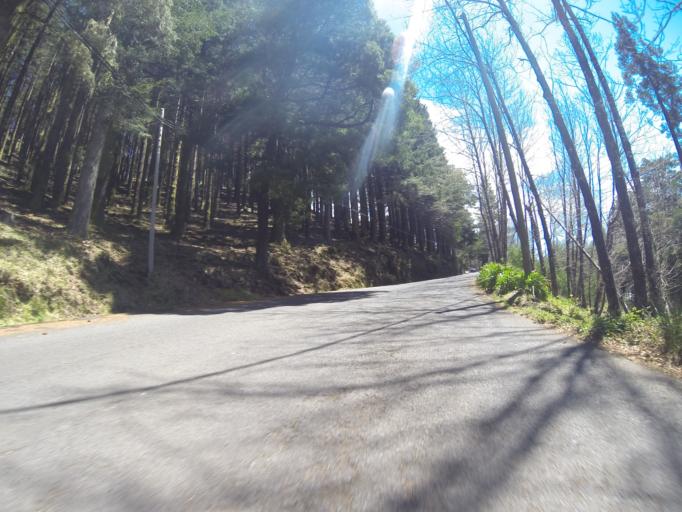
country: PT
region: Madeira
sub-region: Funchal
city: Nossa Senhora do Monte
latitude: 32.7084
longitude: -16.8893
